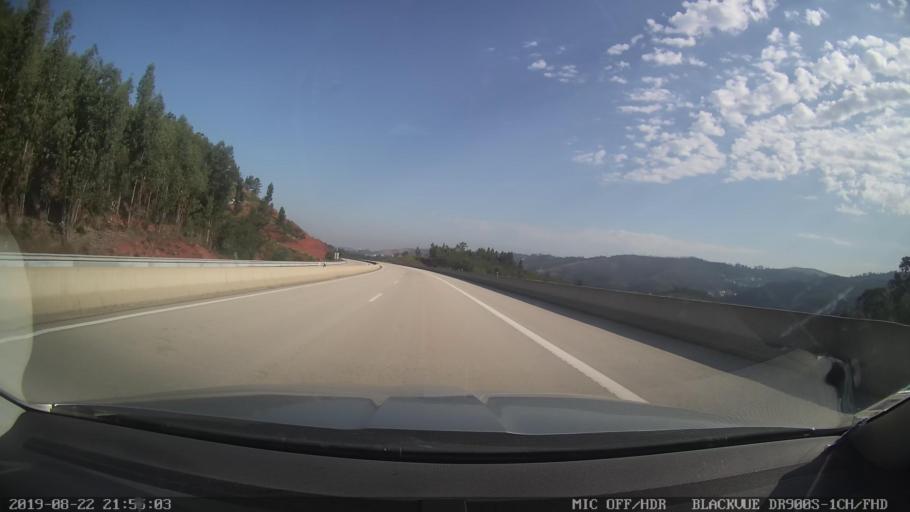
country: PT
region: Coimbra
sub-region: Coimbra
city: Coimbra
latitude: 40.1465
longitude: -8.3830
